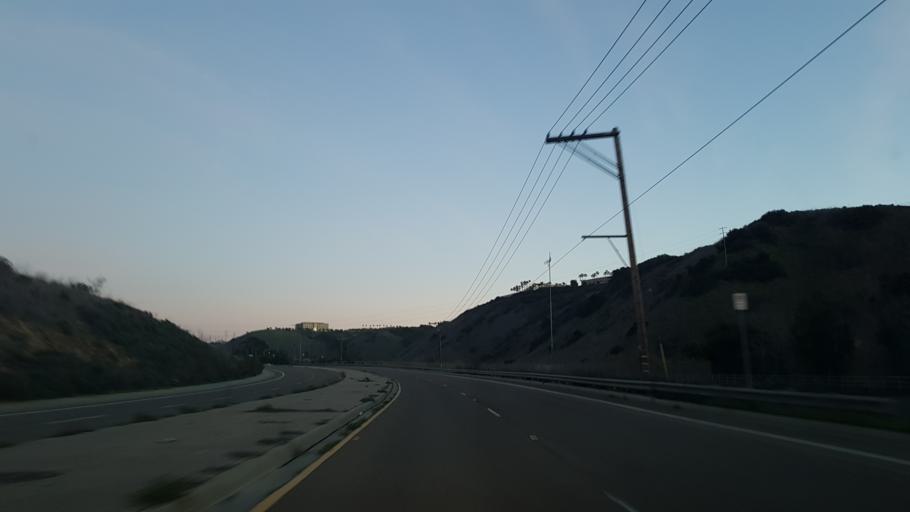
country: US
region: California
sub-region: San Diego County
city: La Jolla
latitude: 32.8940
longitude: -117.2163
